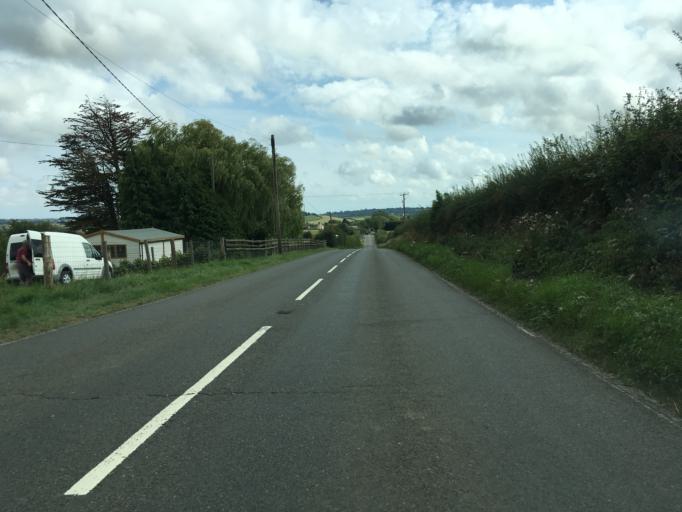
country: GB
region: England
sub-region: Kent
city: Tenterden
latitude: 51.0487
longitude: 0.7356
